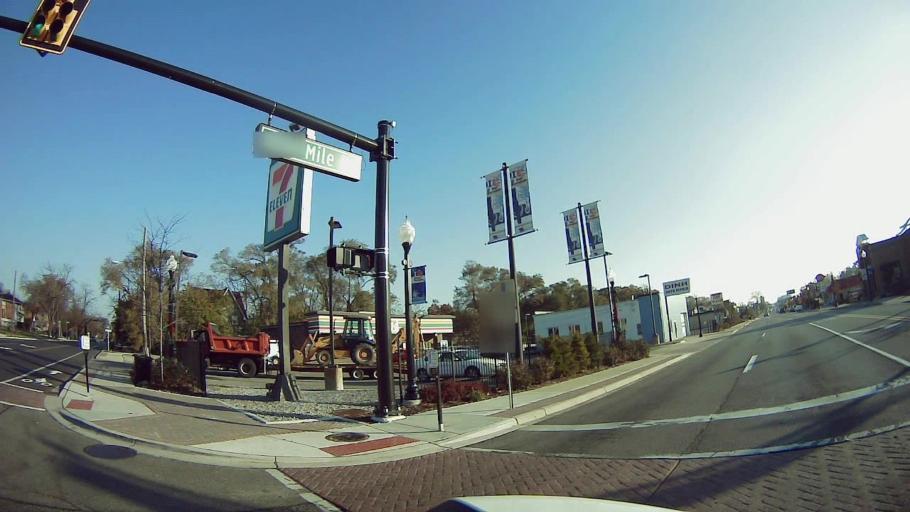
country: US
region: Michigan
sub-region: Oakland County
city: Pleasant Ridge
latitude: 42.4603
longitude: -83.1471
